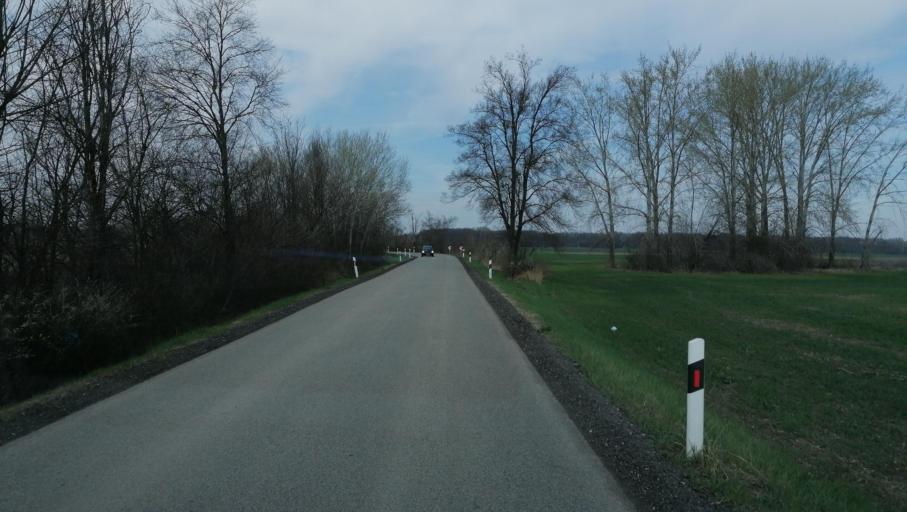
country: HU
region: Pest
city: Kiskunlachaza
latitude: 47.1919
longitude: 18.9719
